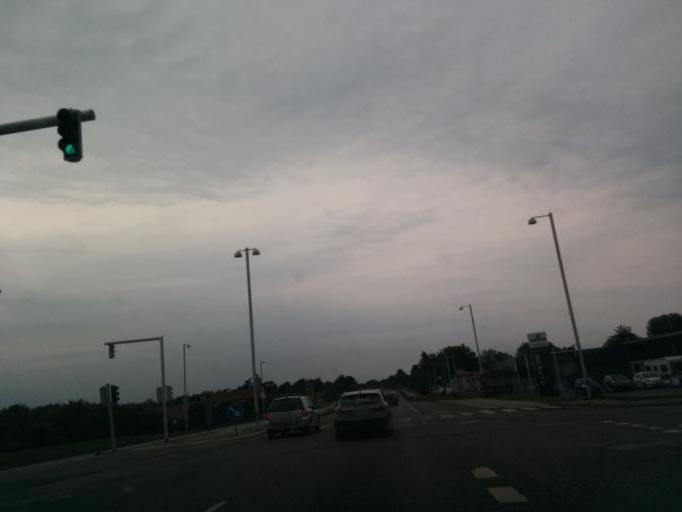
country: DK
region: Central Jutland
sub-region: Arhus Kommune
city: Hjortshoj
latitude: 56.2239
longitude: 10.2890
